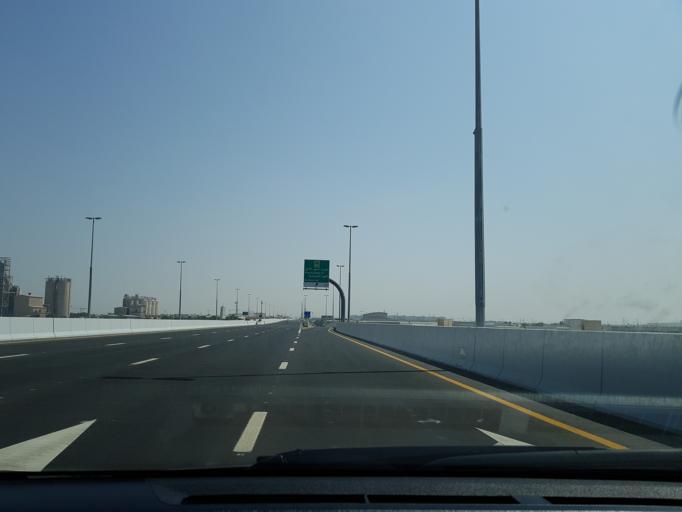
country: AE
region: Dubai
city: Dubai
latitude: 25.1577
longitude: 55.2321
